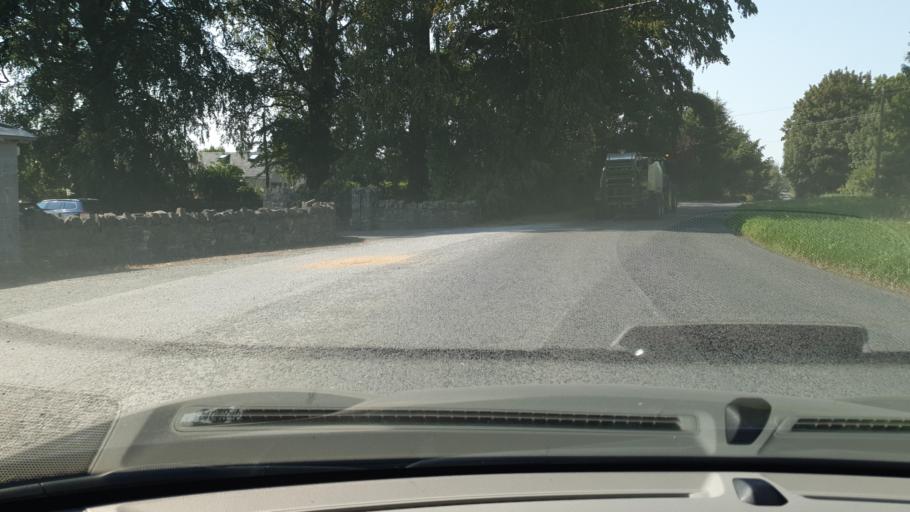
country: IE
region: Leinster
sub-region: An Mhi
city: Athboy
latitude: 53.6031
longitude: -6.8841
